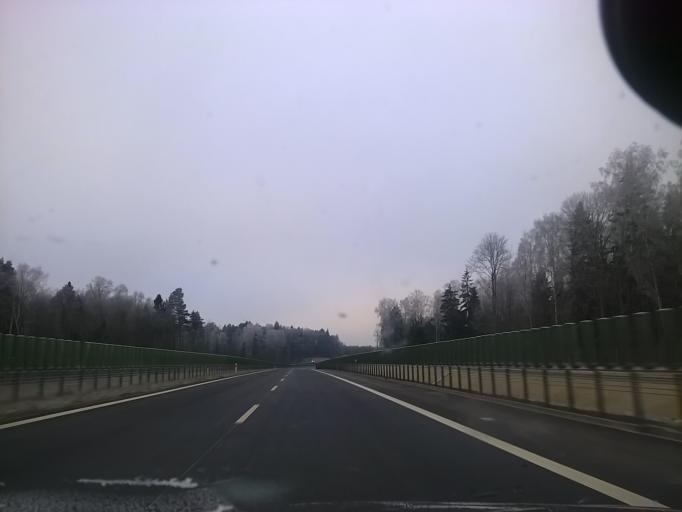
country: PL
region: Warmian-Masurian Voivodeship
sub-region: Powiat olsztynski
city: Biskupiec
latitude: 53.8336
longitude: 21.0872
